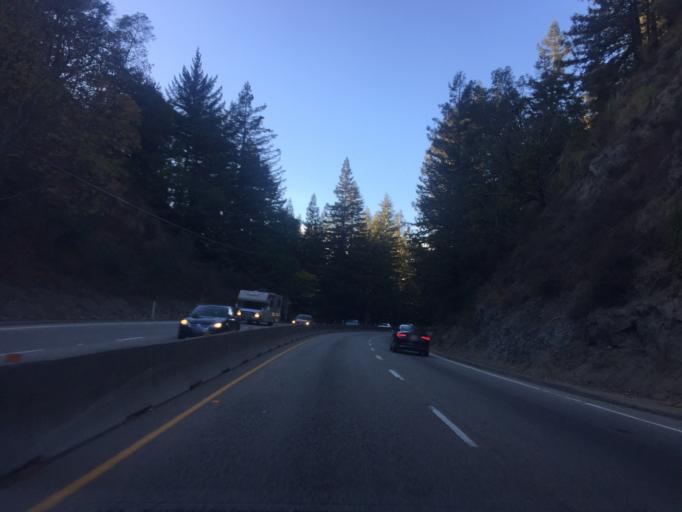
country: US
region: California
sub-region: Santa Cruz County
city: Scotts Valley
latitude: 37.0910
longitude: -121.9779
